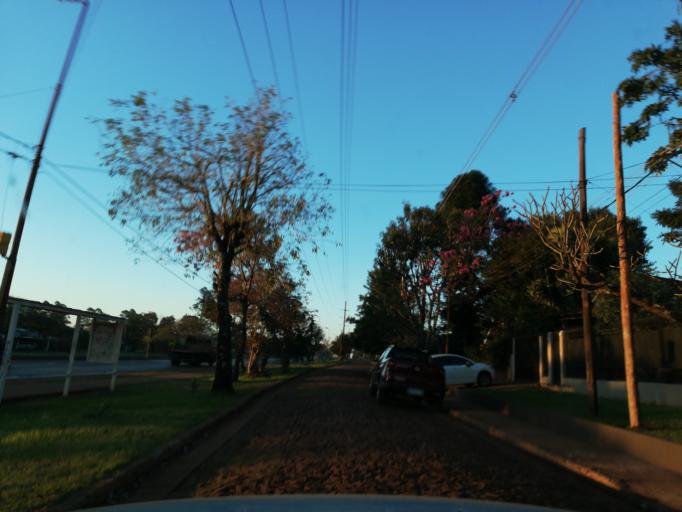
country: AR
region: Misiones
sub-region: Departamento de Capital
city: Posadas
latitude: -27.4177
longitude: -55.9297
